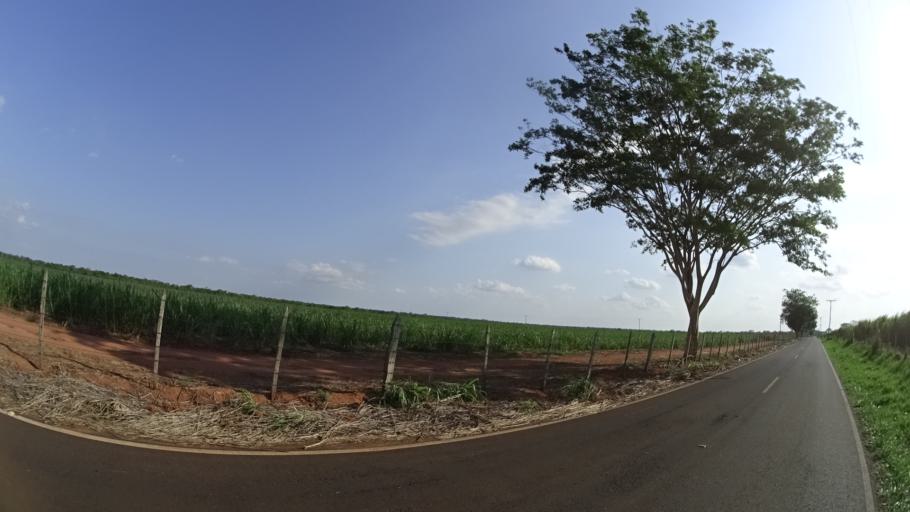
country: BR
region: Sao Paulo
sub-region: Urupes
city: Urupes
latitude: -21.3884
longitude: -49.5000
